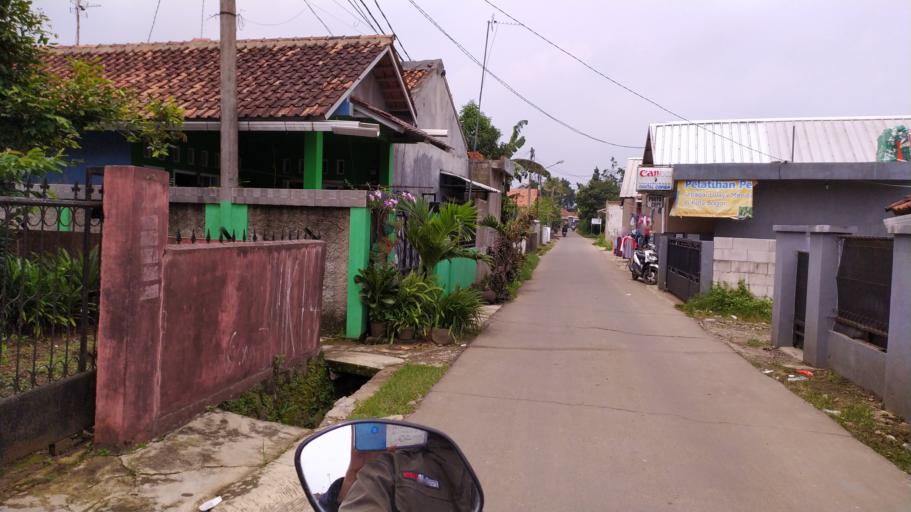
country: ID
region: West Java
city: Ciampea
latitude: -6.5796
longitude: 106.7265
